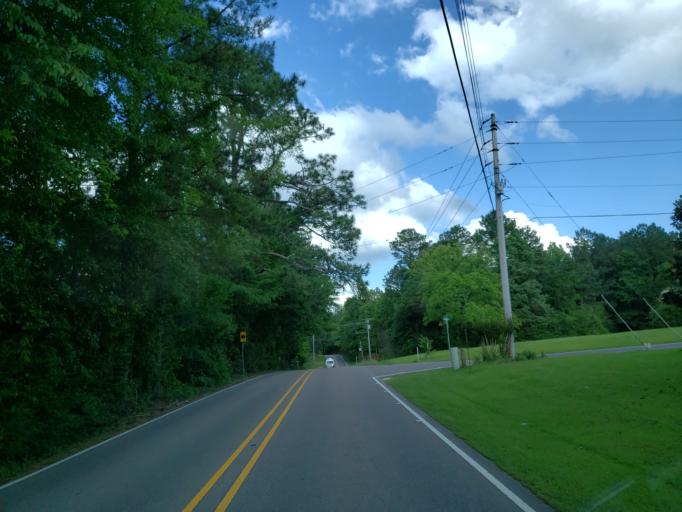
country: US
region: Mississippi
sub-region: Lamar County
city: West Hattiesburg
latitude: 31.2737
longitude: -89.3829
